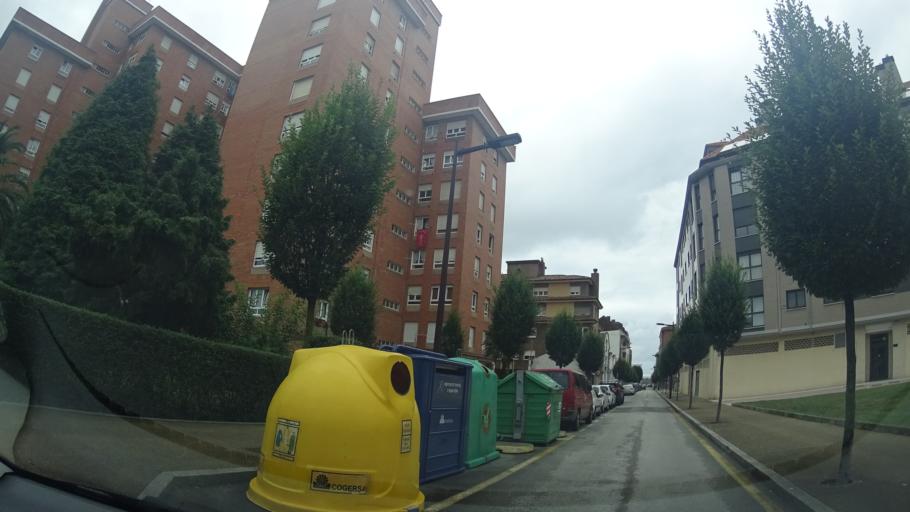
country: ES
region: Asturias
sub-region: Province of Asturias
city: Natahoyo
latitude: 43.5385
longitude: -5.6819
